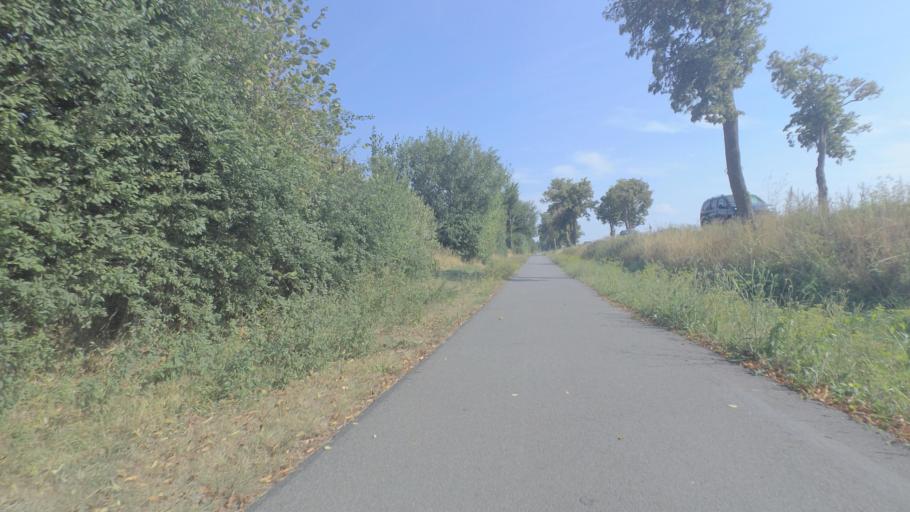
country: DE
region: Mecklenburg-Vorpommern
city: Grimmen
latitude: 54.0987
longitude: 13.0741
